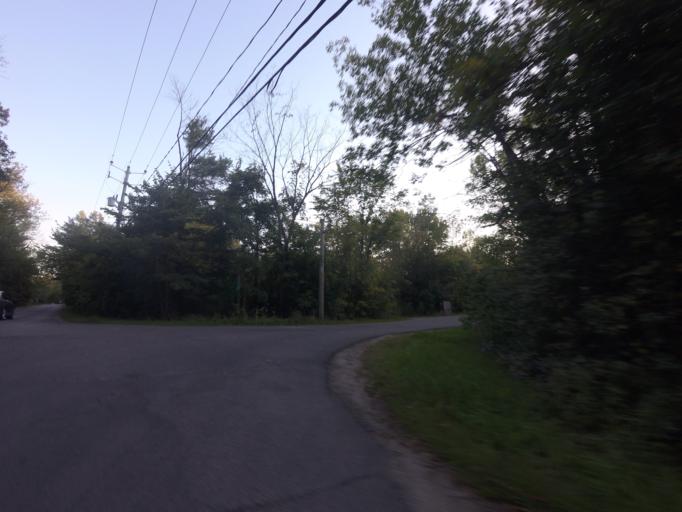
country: CA
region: Quebec
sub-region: Laurentides
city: Oka
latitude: 45.4449
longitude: -74.1068
